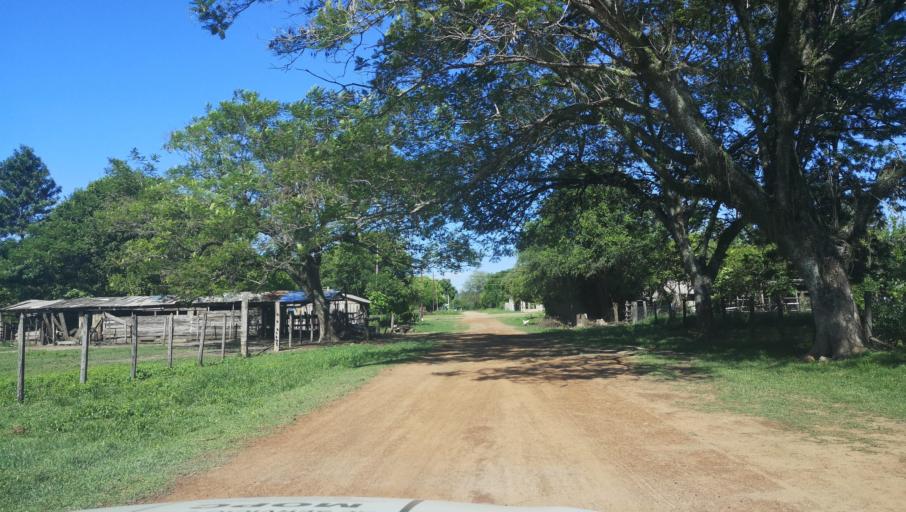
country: PY
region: Caaguazu
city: Carayao
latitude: -25.1938
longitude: -56.4003
